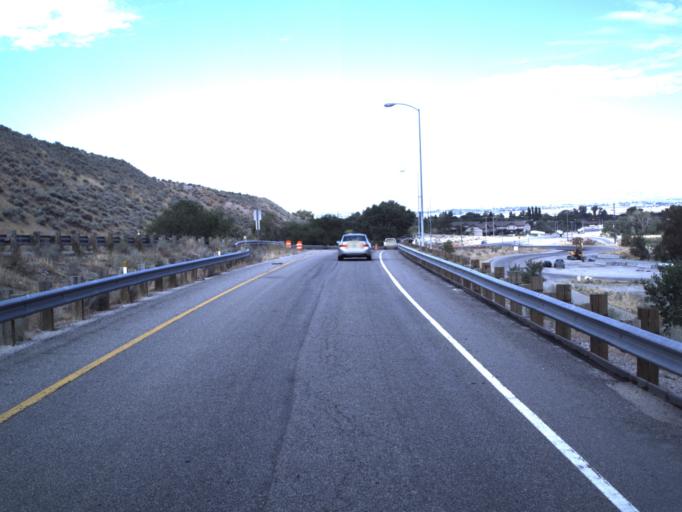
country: US
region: Utah
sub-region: Box Elder County
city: Brigham City
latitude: 41.5003
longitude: -111.9944
